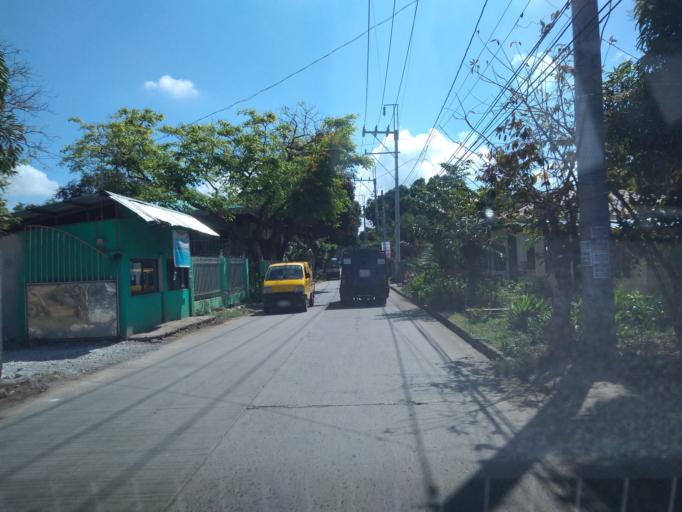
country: PH
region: Central Luzon
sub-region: Province of Bulacan
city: Bitungol
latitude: 14.8599
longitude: 121.0371
